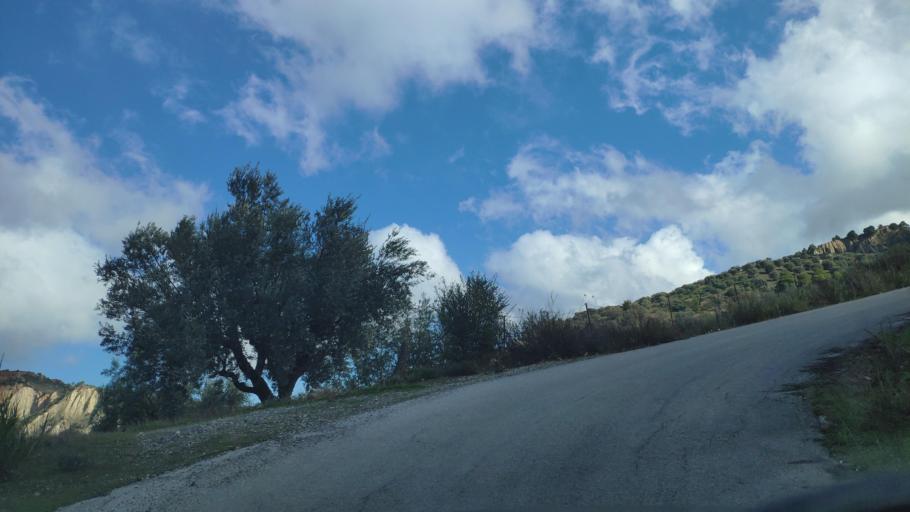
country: GR
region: West Greece
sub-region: Nomos Achaias
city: Aiyira
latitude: 38.1086
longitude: 22.4402
